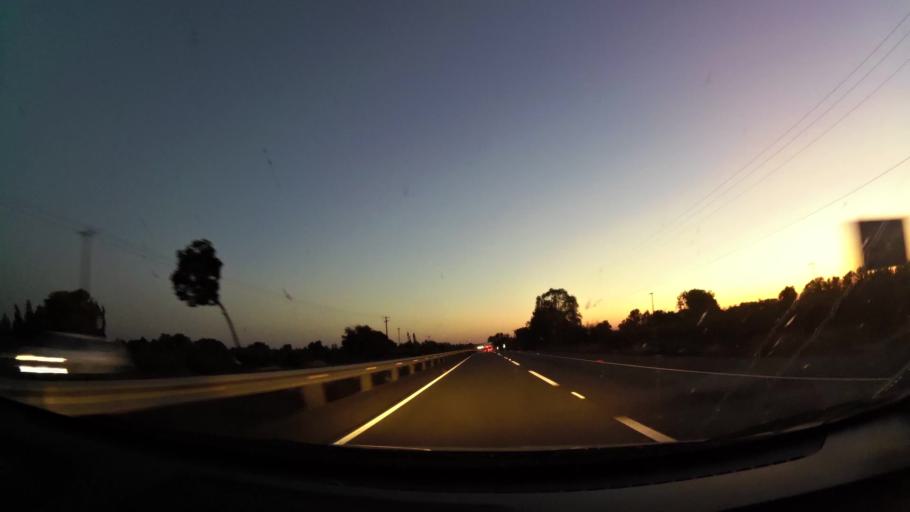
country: CL
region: Biobio
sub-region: Provincia de Nuble
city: San Carlos
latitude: -36.3177
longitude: -71.8354
